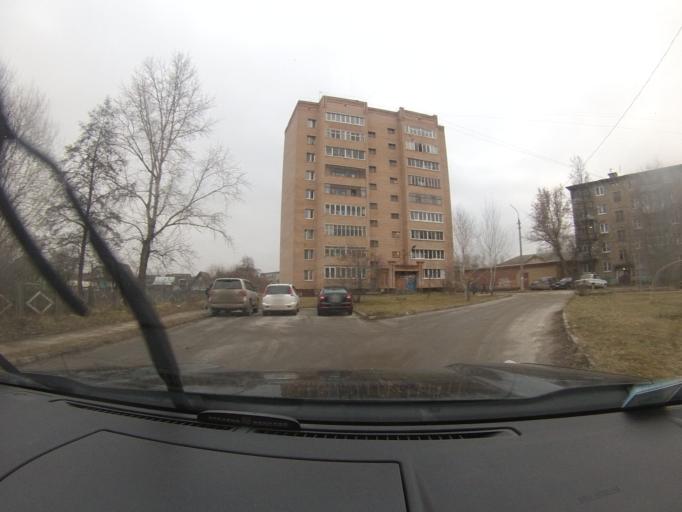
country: RU
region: Moskovskaya
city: Peski
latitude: 55.2476
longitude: 38.7668
